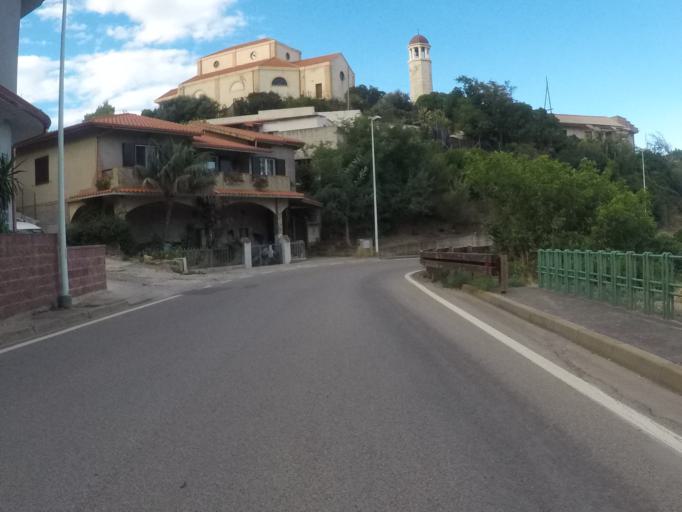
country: IT
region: Sardinia
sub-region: Provincia di Carbonia-Iglesias
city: Gonnesa
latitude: 39.3160
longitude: 8.4374
